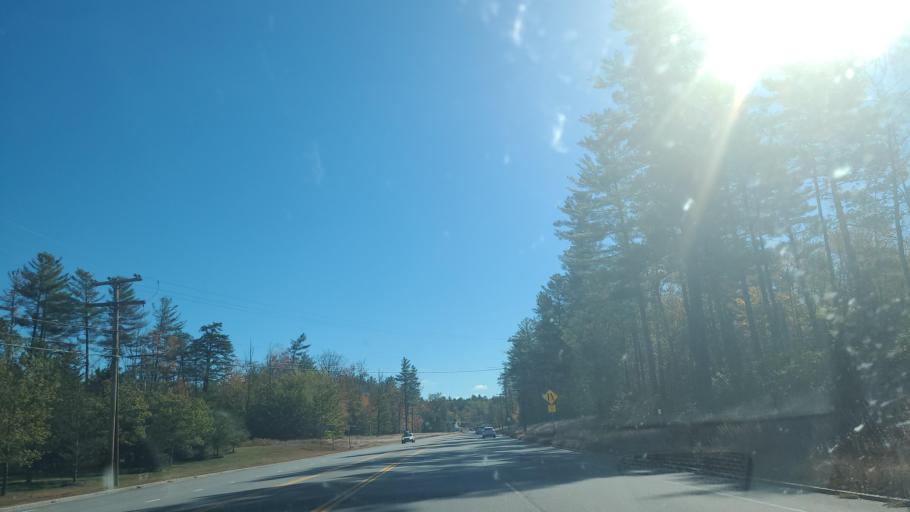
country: US
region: New Hampshire
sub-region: Carroll County
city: Conway
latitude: 44.0159
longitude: -71.1072
